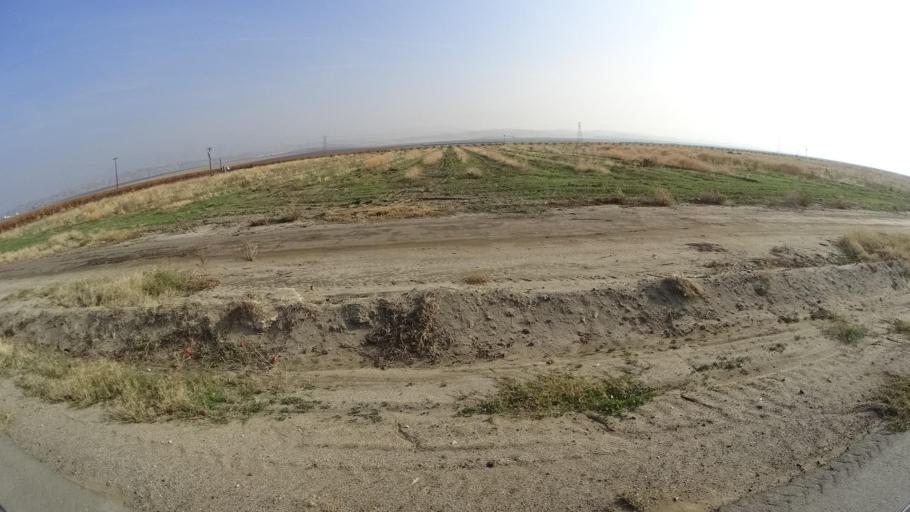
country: US
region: California
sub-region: Kern County
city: Arvin
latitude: 35.0738
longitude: -118.8465
